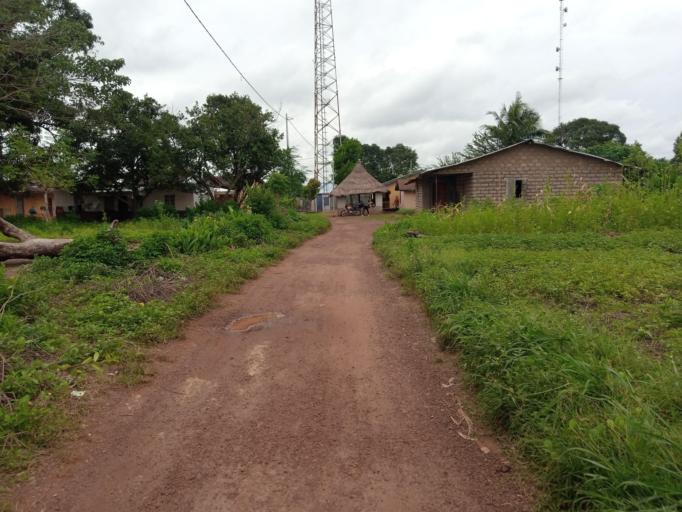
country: SL
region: Southern Province
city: Largo
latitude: 8.2011
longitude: -12.0587
